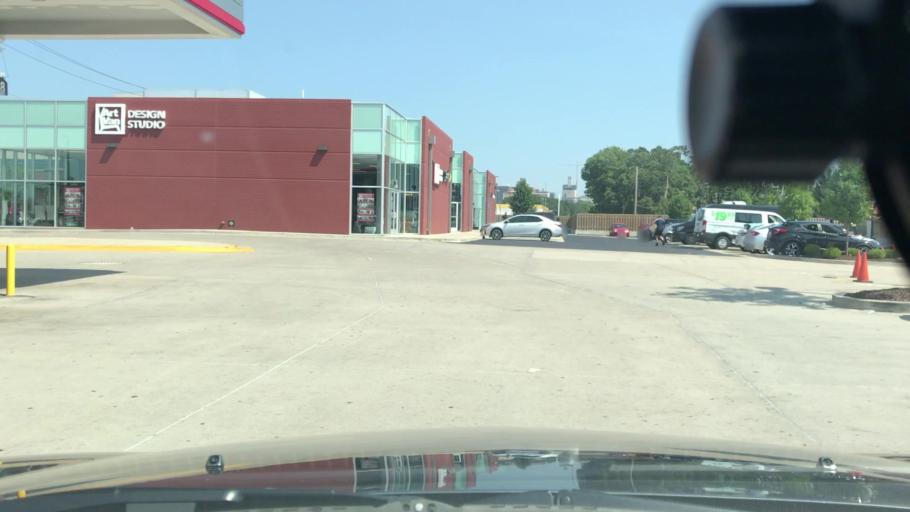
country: US
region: Missouri
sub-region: Saint Louis County
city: Richmond Heights
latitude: 38.6257
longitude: -90.3345
